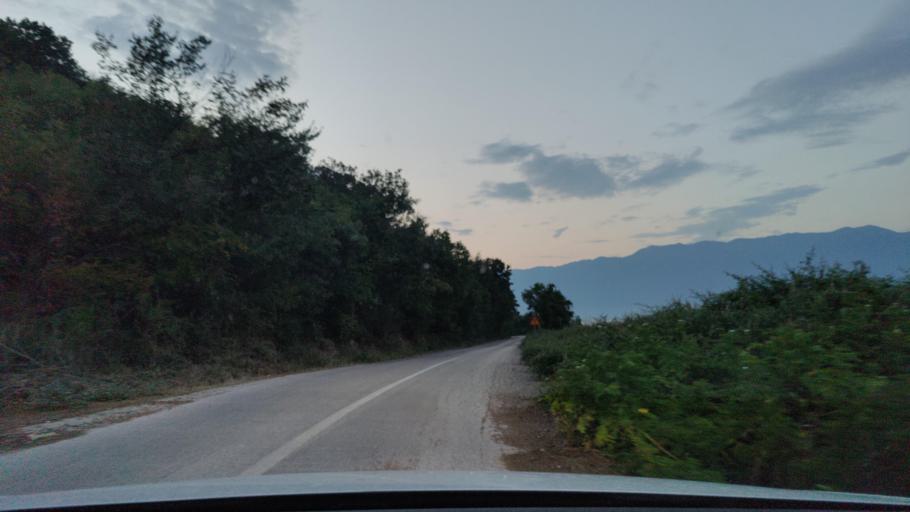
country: GR
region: Central Macedonia
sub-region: Nomos Serron
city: Chrysochorafa
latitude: 41.1627
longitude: 23.1840
